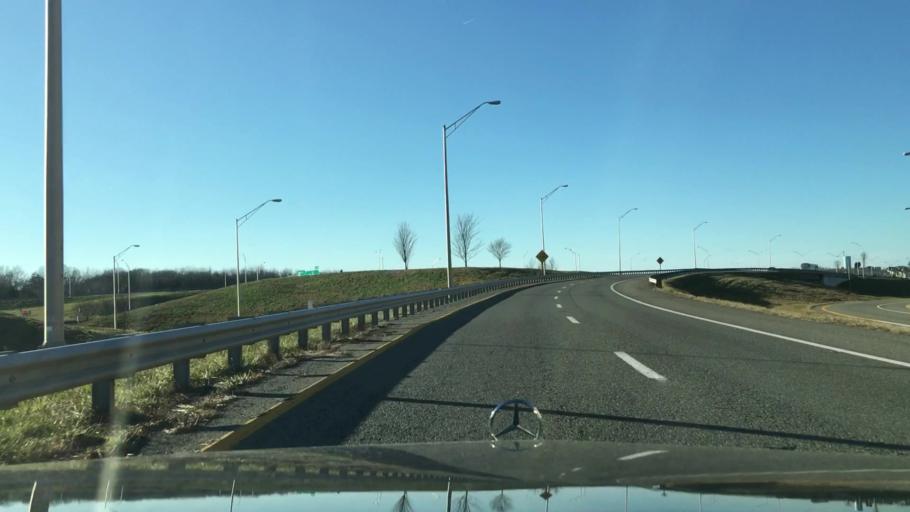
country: US
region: Virginia
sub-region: Montgomery County
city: Christiansburg
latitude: 37.1310
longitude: -80.3693
